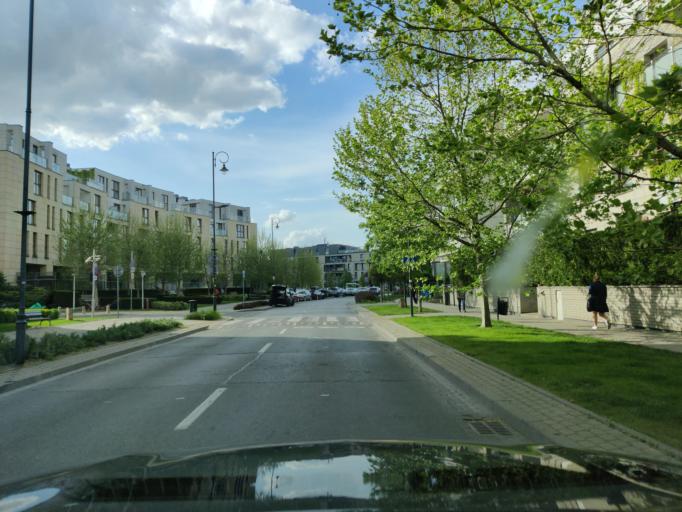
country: PL
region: Masovian Voivodeship
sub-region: Warszawa
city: Wilanow
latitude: 52.1637
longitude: 21.0751
